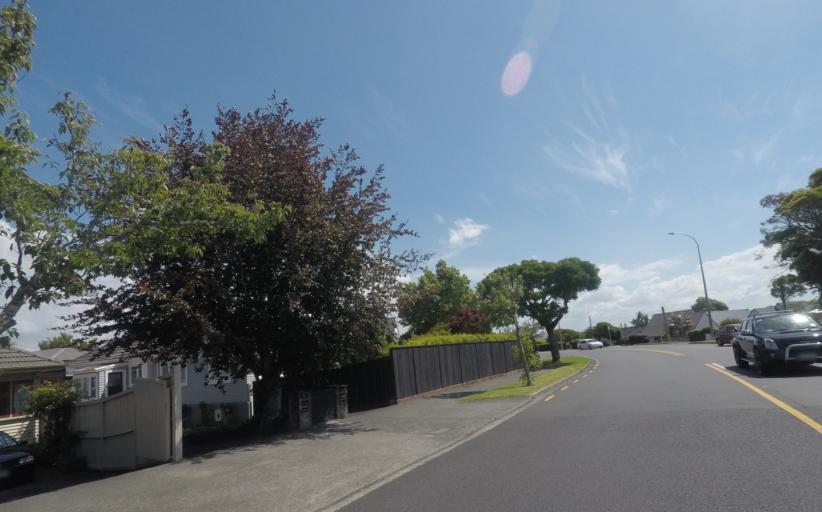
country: NZ
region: Auckland
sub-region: Auckland
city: Tamaki
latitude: -36.8735
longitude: 174.8295
